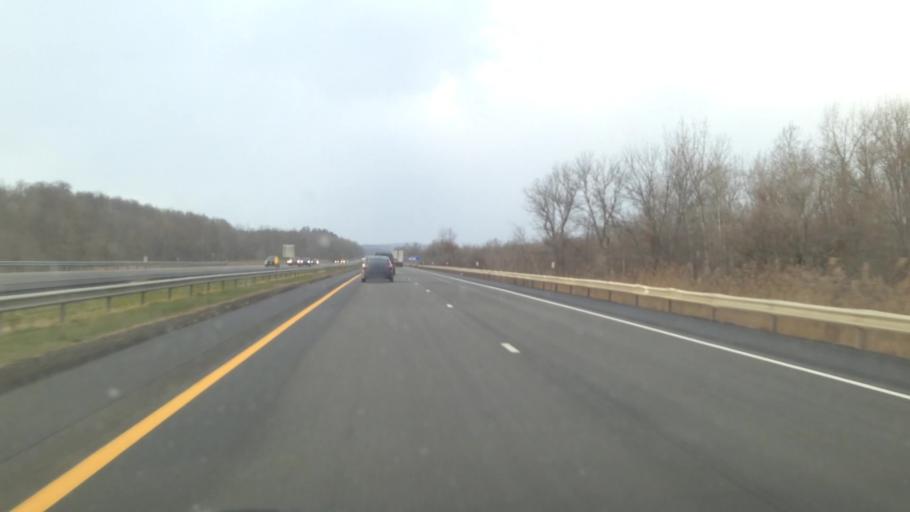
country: US
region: New York
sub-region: Montgomery County
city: Tribes Hill
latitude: 42.9349
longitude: -74.3238
